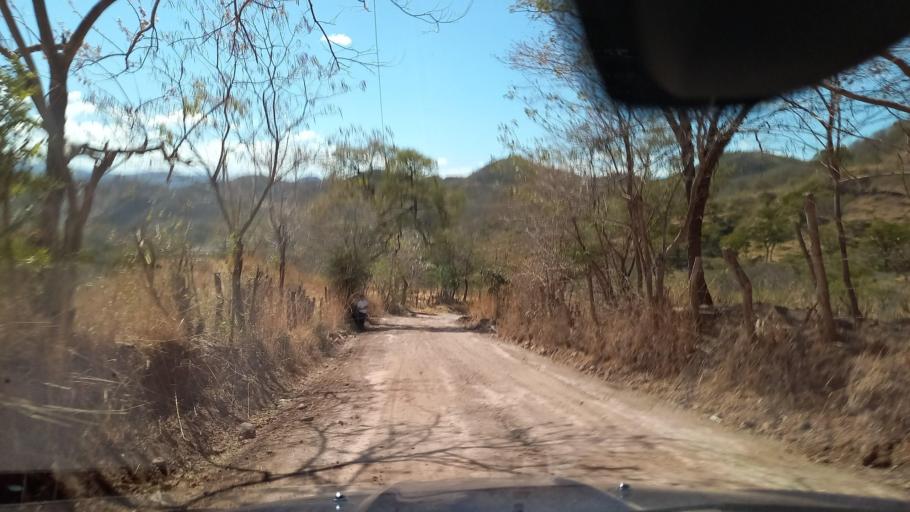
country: SV
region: Santa Ana
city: Metapan
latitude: 14.3646
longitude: -89.4977
